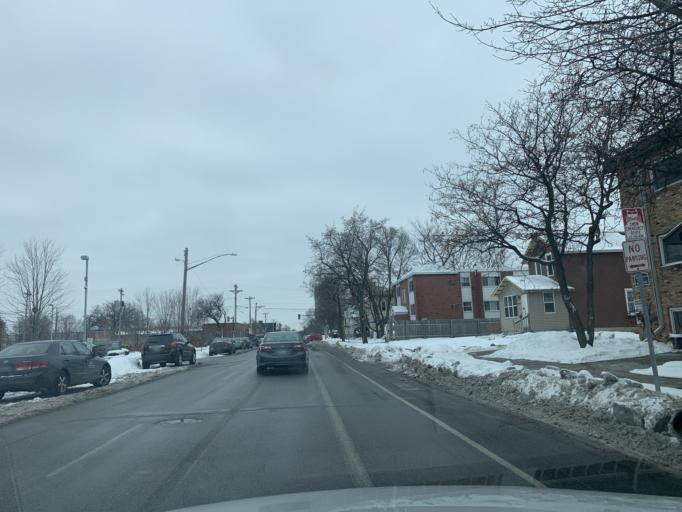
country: US
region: Minnesota
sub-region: Hennepin County
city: Minneapolis
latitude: 44.9518
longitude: -93.2797
